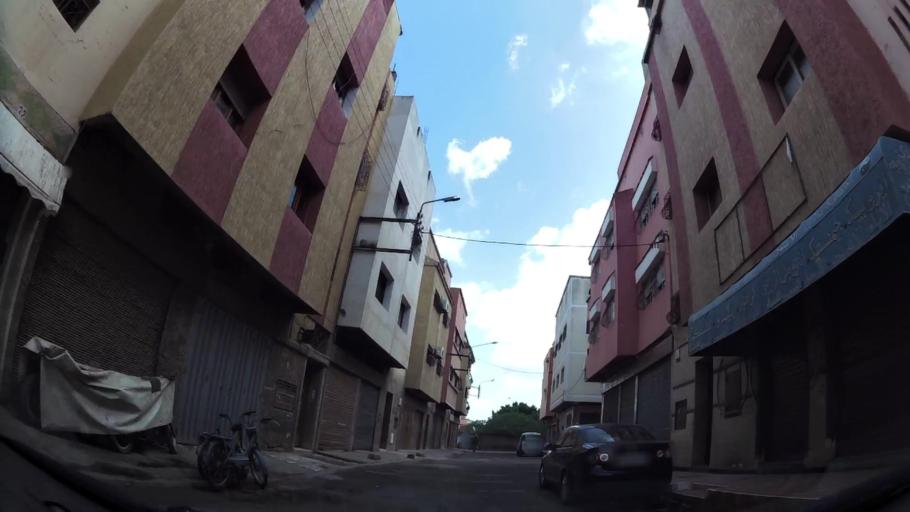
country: MA
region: Grand Casablanca
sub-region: Casablanca
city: Casablanca
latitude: 33.5413
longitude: -7.5904
